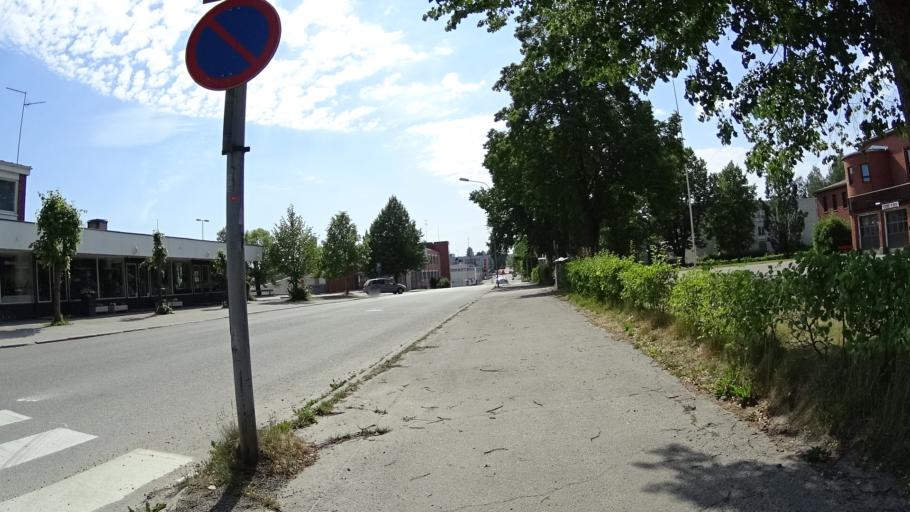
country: FI
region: Uusimaa
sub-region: Raaseporin
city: Karis
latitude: 60.0722
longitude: 23.6643
